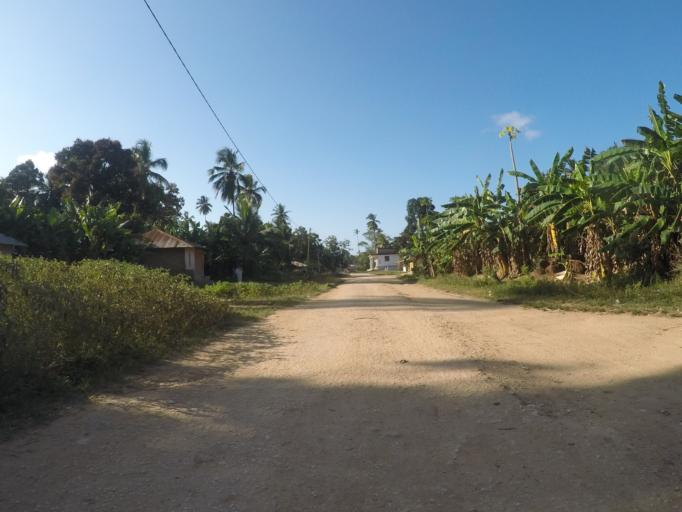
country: TZ
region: Zanzibar Central/South
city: Koani
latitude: -6.1576
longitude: 39.2873
